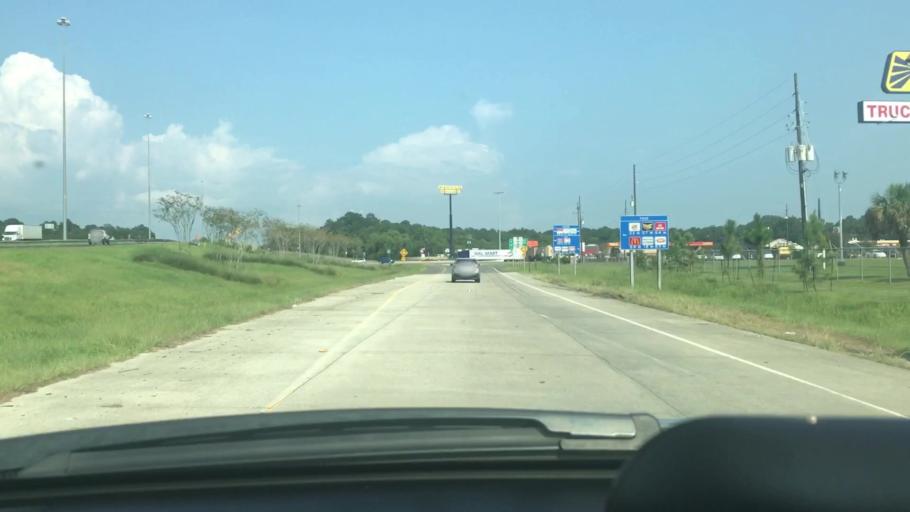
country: US
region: Louisiana
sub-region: Tangipahoa Parish
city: Hammond
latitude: 30.4787
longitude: -90.4594
